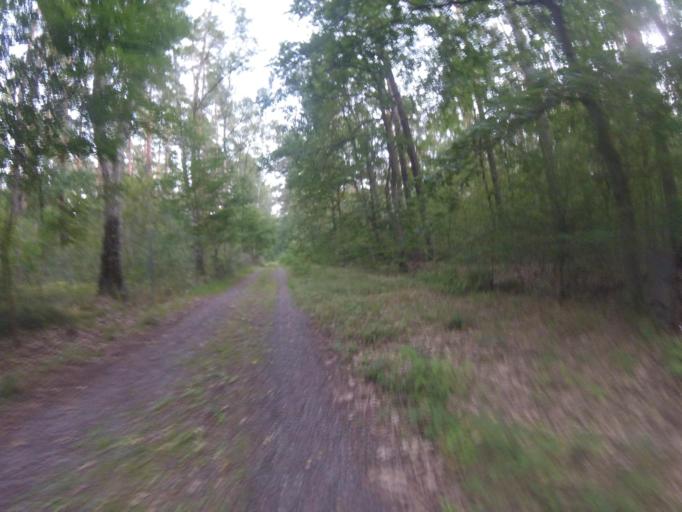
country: DE
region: Berlin
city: Bohnsdorf
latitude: 52.3899
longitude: 13.5925
